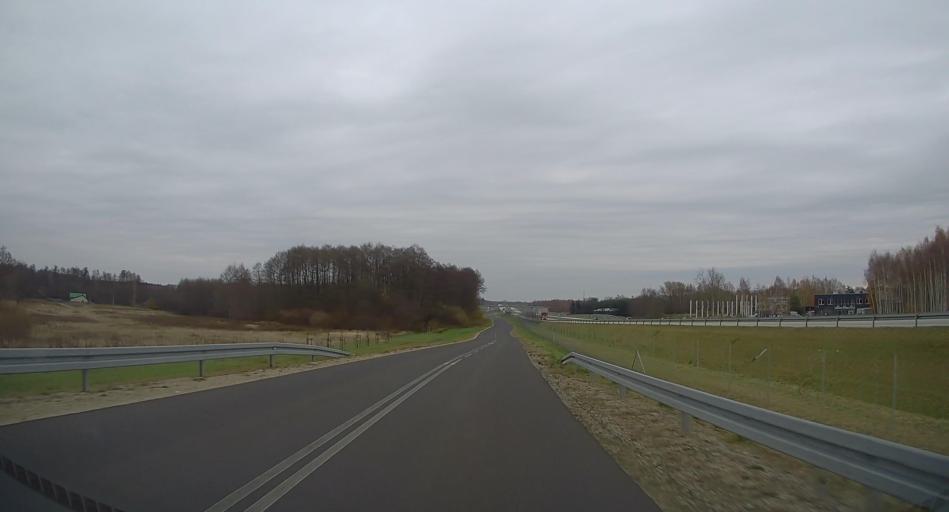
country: PL
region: Masovian Voivodeship
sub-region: Powiat zyrardowski
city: Radziejowice
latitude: 52.0145
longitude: 20.6189
